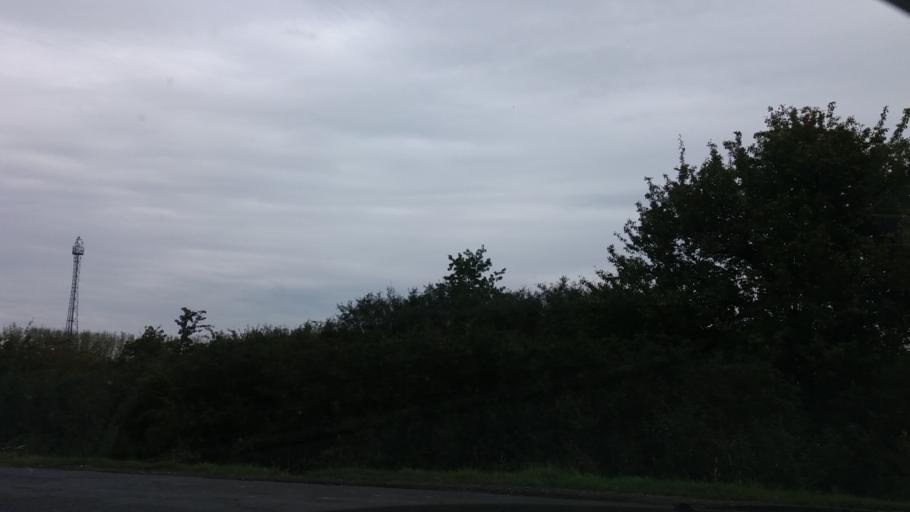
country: PL
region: Lower Silesian Voivodeship
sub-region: Powiat legnicki
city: Legnickie Pole
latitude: 51.1303
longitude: 16.3417
